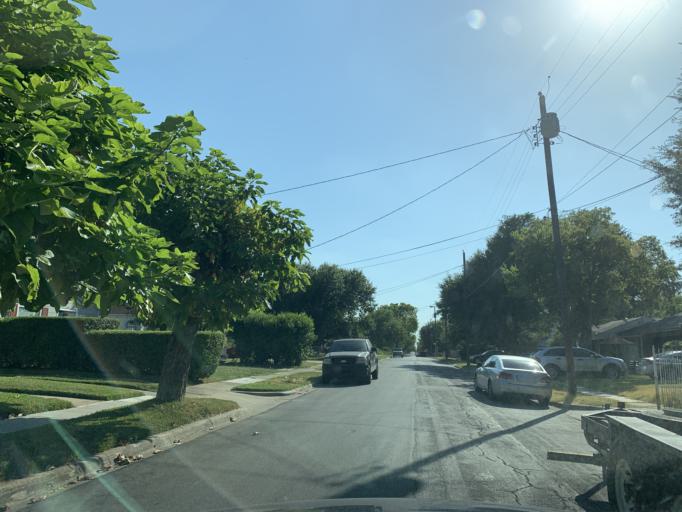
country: US
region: Texas
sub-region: Dallas County
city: Dallas
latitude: 32.7065
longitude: -96.7901
